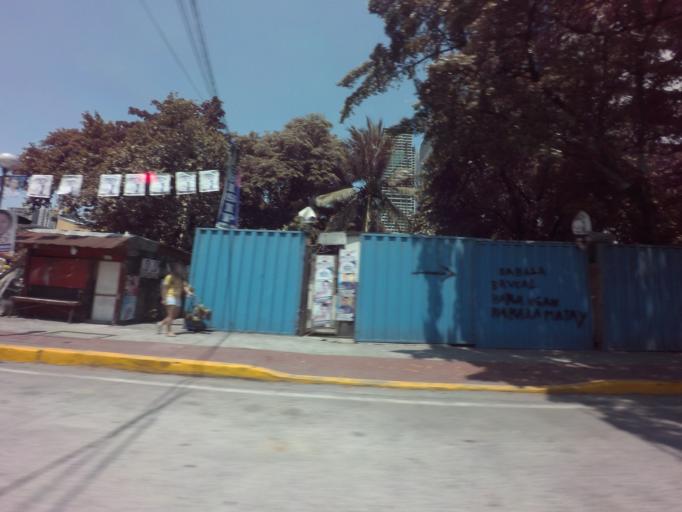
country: PH
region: Metro Manila
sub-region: Makati City
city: Makati City
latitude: 14.5628
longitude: 120.9985
